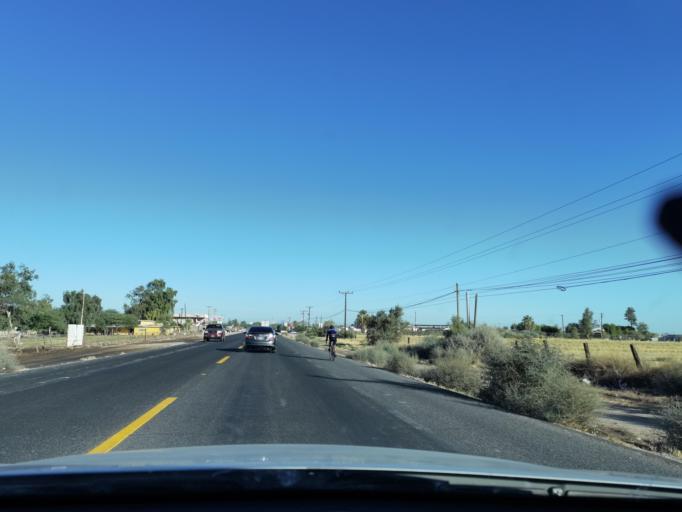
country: MX
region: Baja California
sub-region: Mexicali
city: Islas Agrarias Grupo A
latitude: 32.6465
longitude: -115.3242
